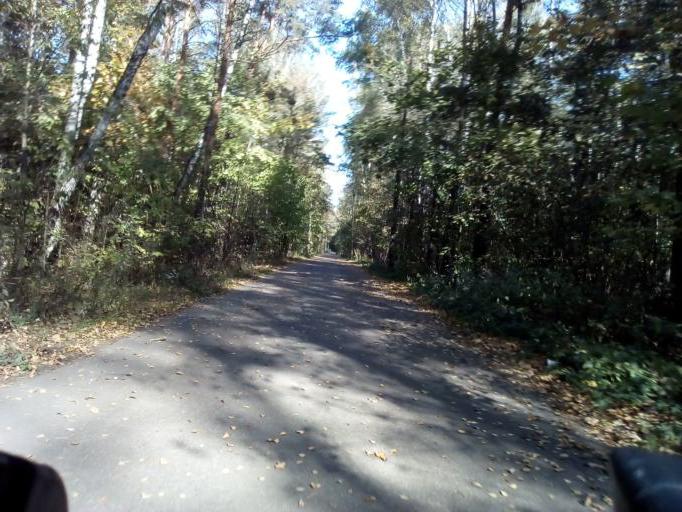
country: RU
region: Moskovskaya
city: Malyshevo
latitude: 55.5481
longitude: 38.3024
